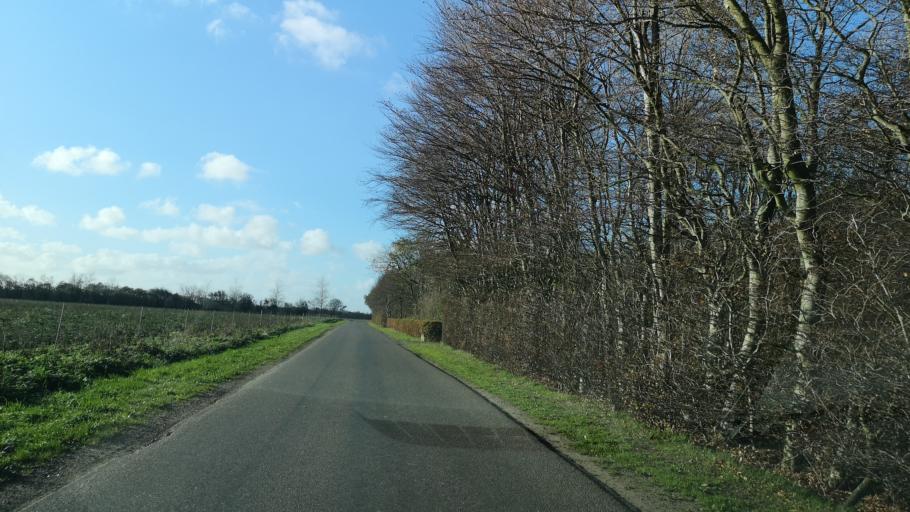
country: DK
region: Central Jutland
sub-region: Ringkobing-Skjern Kommune
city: Tarm
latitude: 55.8294
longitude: 8.3861
